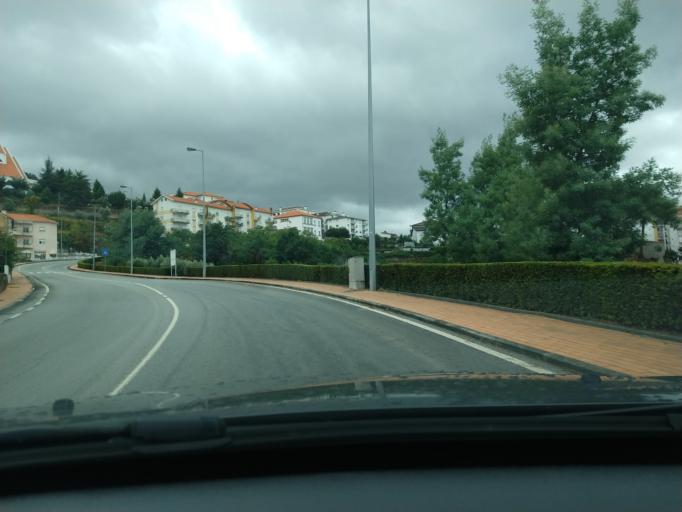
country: PT
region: Guarda
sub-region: Seia
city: Seia
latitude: 40.4038
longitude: -7.7116
